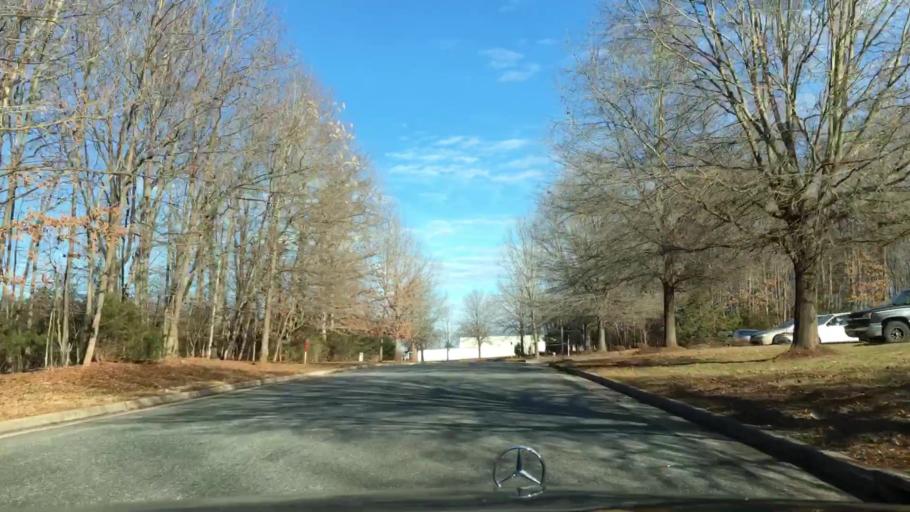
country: US
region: Virginia
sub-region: Bedford County
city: Forest
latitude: 37.3724
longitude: -79.2359
